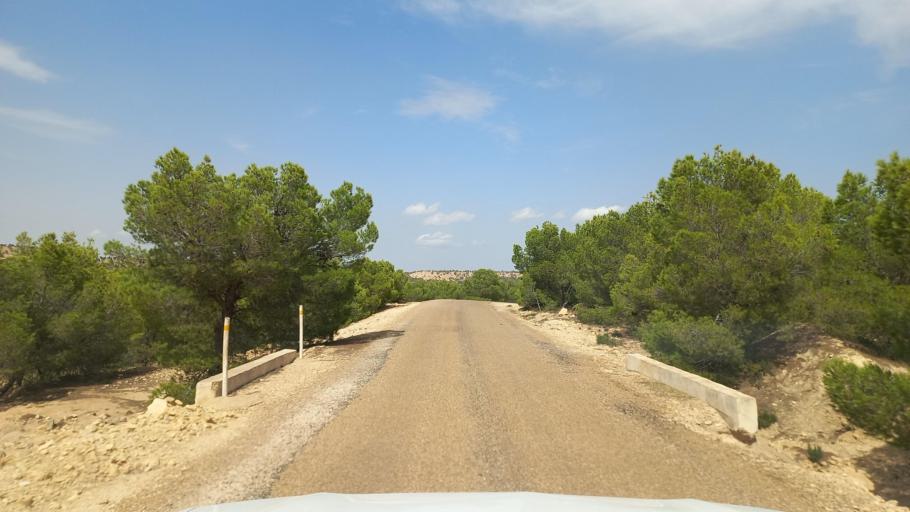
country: TN
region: Al Qasrayn
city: Sbiba
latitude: 35.4033
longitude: 8.9205
